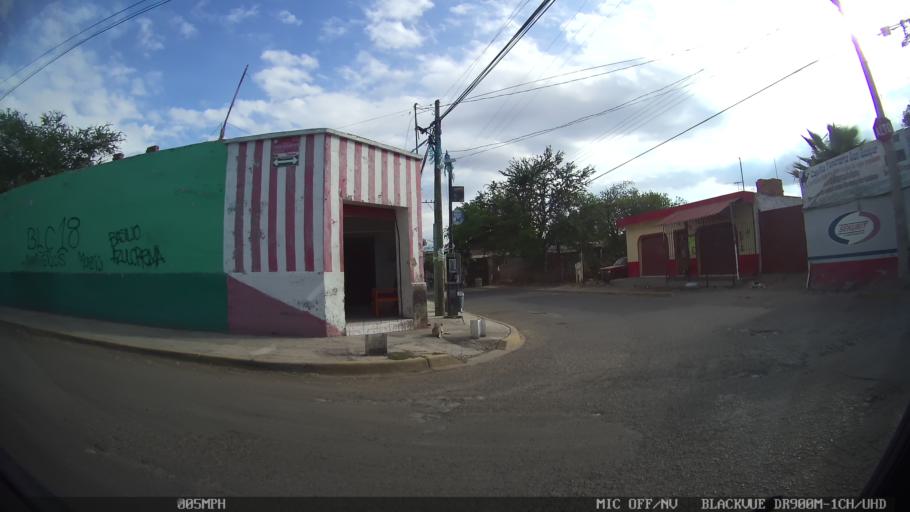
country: MX
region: Jalisco
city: Tonala
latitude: 20.6785
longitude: -103.2449
